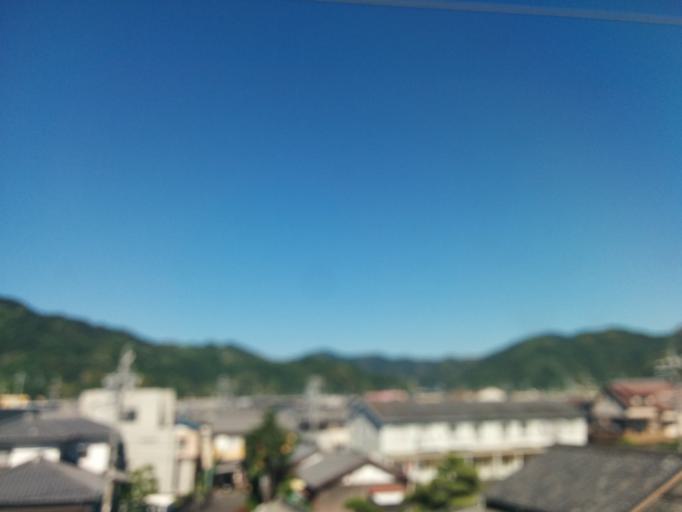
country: JP
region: Shizuoka
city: Shizuoka-shi
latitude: 34.9430
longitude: 138.3632
